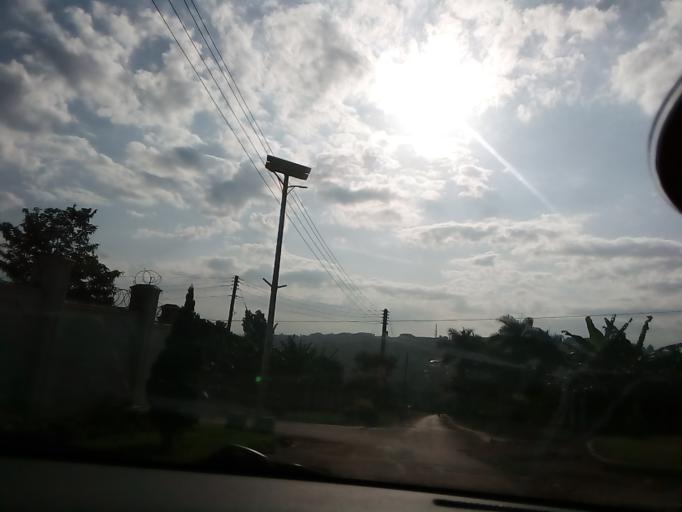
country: UG
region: Central Region
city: Masaka
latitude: -0.3508
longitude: 31.7406
